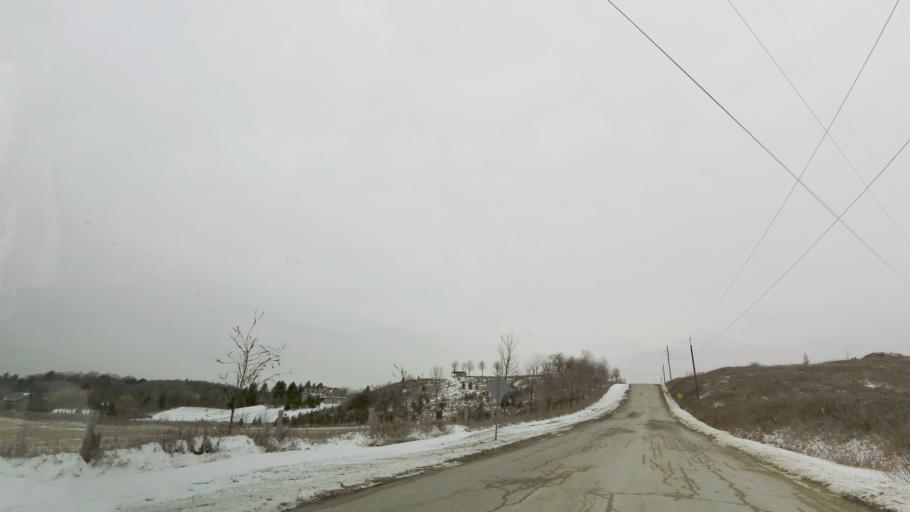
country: CA
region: Ontario
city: Vaughan
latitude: 43.9273
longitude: -79.6069
